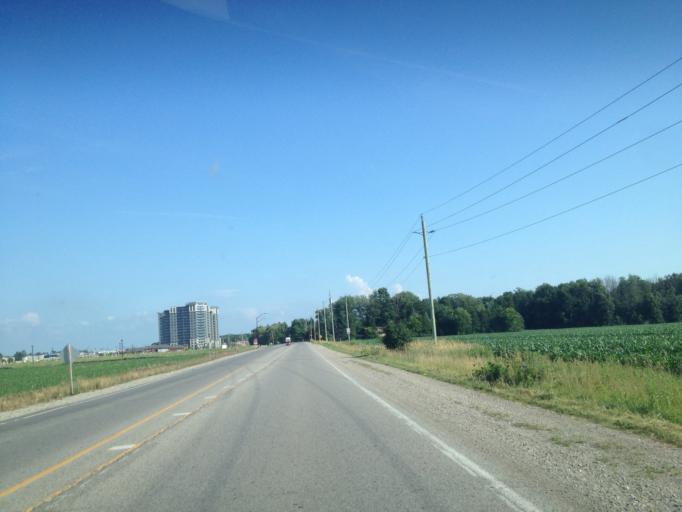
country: CA
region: Ontario
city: London
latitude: 43.0202
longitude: -81.3443
